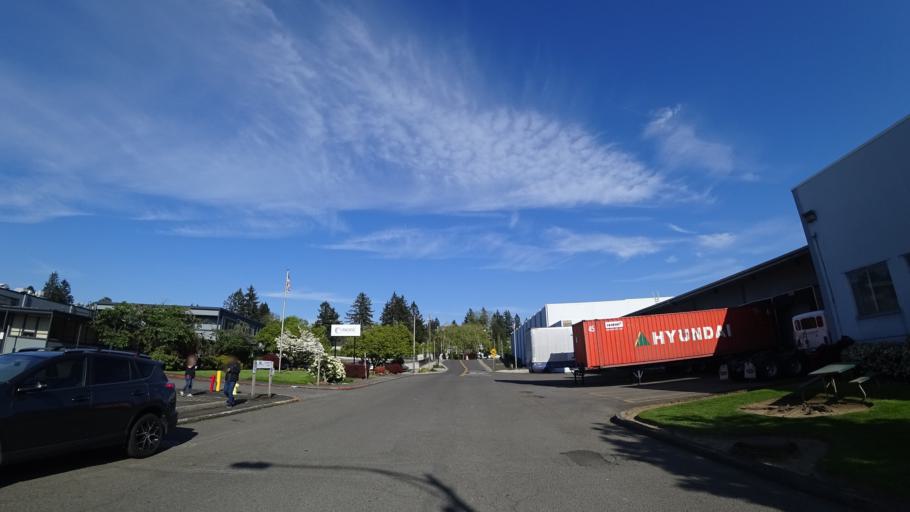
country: US
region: Oregon
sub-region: Clackamas County
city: Milwaukie
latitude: 45.4545
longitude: -122.6375
